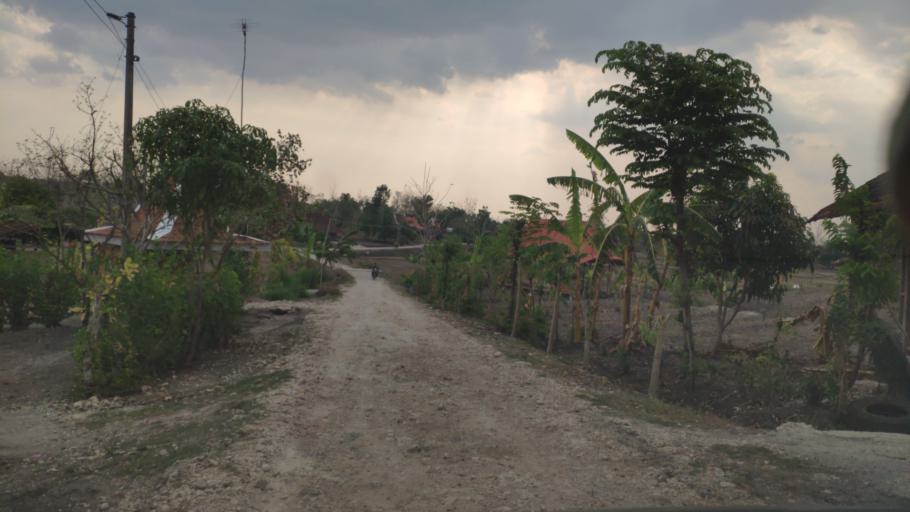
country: ID
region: Central Java
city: Randublatung
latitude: -7.2854
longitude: 111.2698
